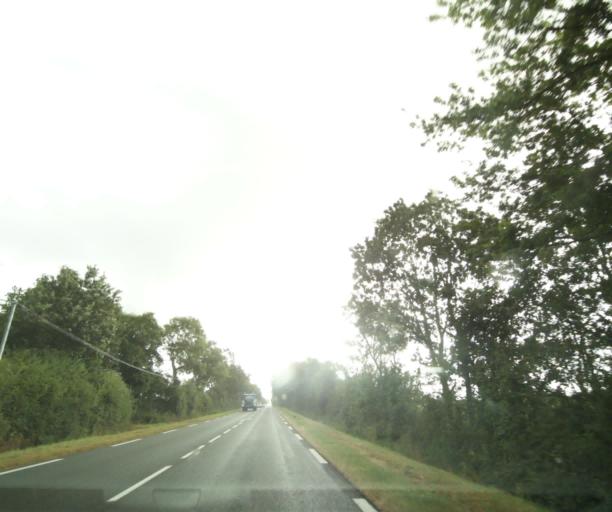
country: FR
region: Pays de la Loire
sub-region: Departement de la Vendee
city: Saint-Hilaire-de-Talmont
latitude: 46.4719
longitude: -1.5498
